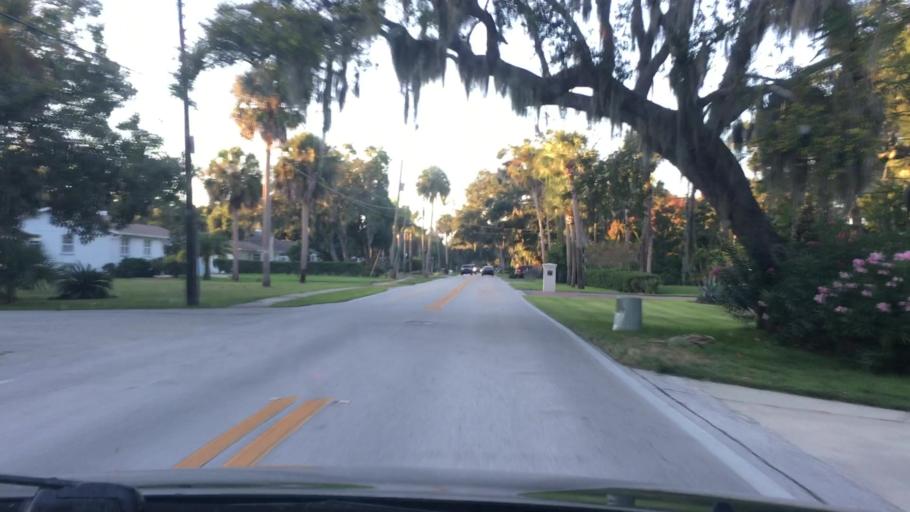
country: US
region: Florida
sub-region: Volusia County
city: Ormond Beach
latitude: 29.2983
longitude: -81.0615
